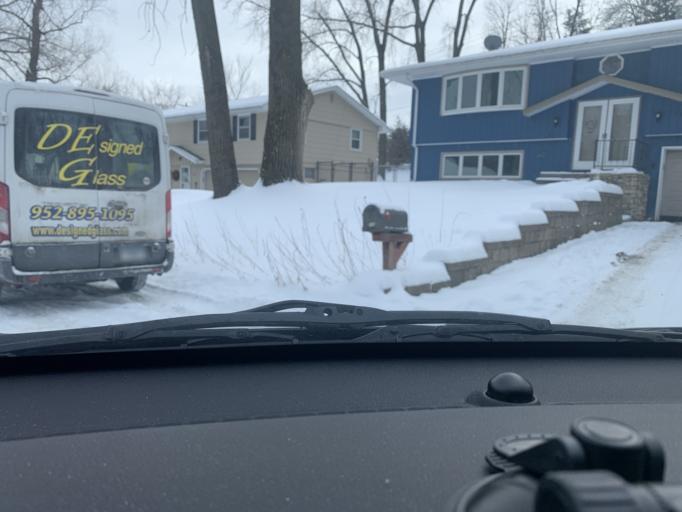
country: US
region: Minnesota
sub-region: Dakota County
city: South Saint Paul
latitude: 44.8840
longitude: -93.0610
